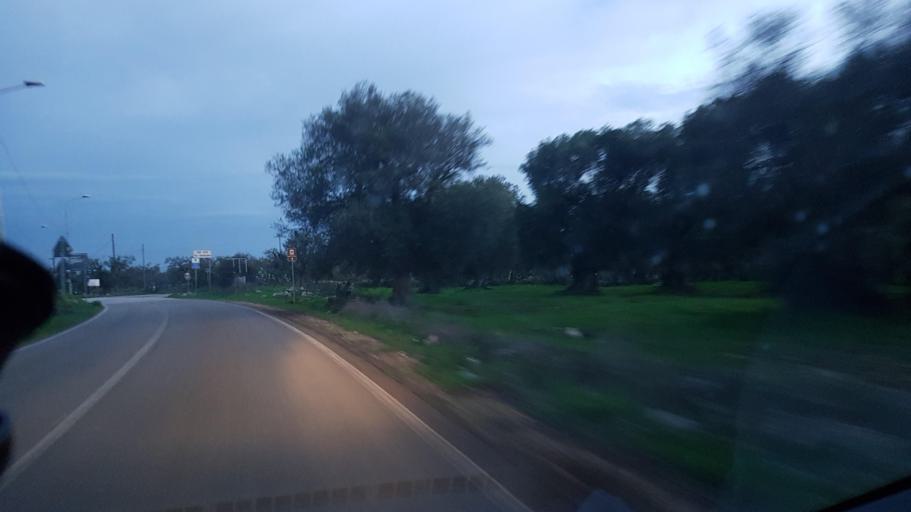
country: IT
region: Apulia
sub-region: Provincia di Brindisi
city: San Vito dei Normanni
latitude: 40.6502
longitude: 17.6929
